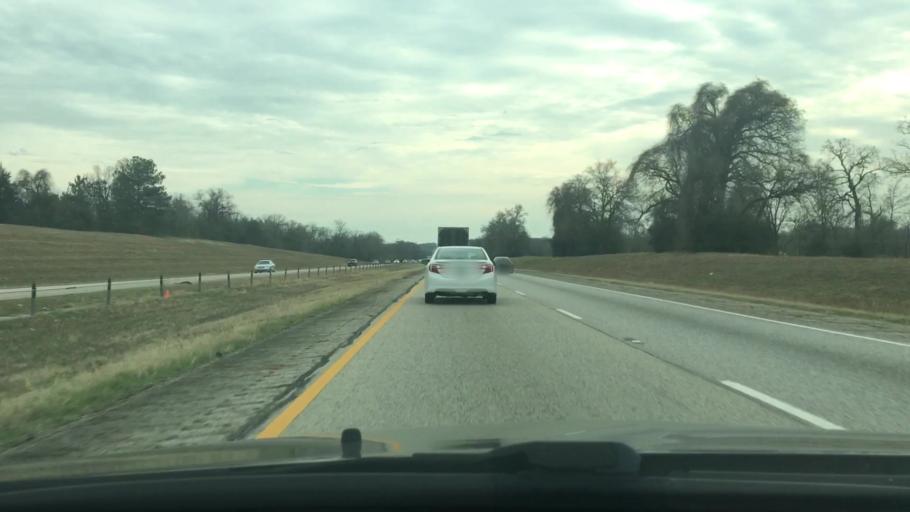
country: US
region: Texas
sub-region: Leon County
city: Centerville
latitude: 31.2030
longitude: -95.9953
